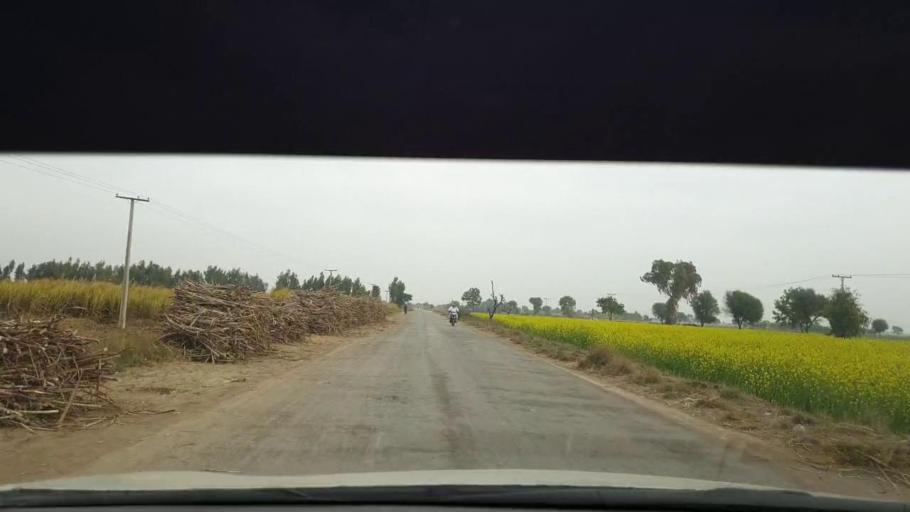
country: PK
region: Sindh
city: Berani
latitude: 25.7768
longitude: 68.8861
